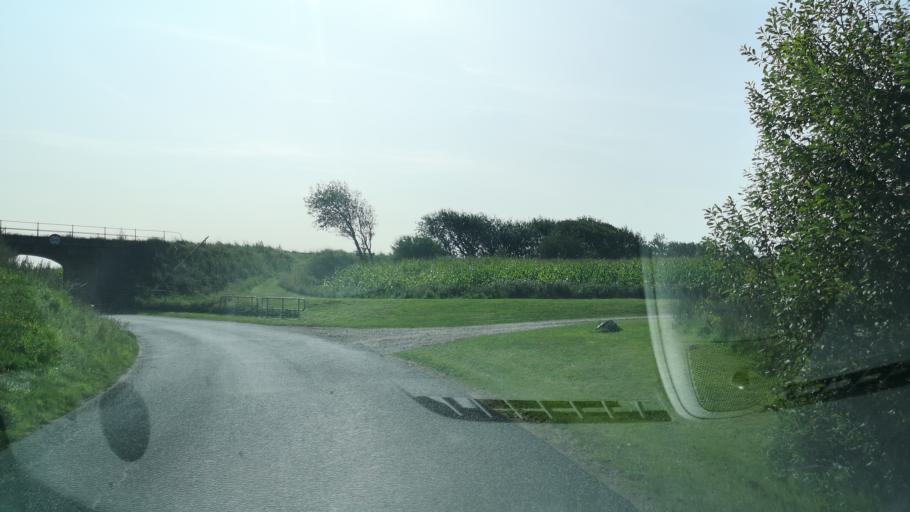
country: DK
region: Central Jutland
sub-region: Ringkobing-Skjern Kommune
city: Videbaek
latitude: 56.0730
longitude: 8.6121
